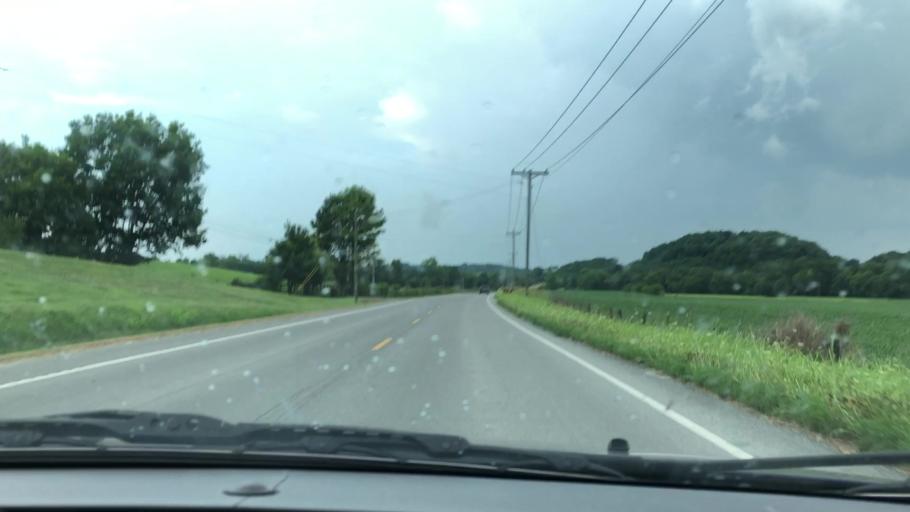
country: US
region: Tennessee
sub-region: Williamson County
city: Thompson's Station
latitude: 35.8339
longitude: -86.9666
